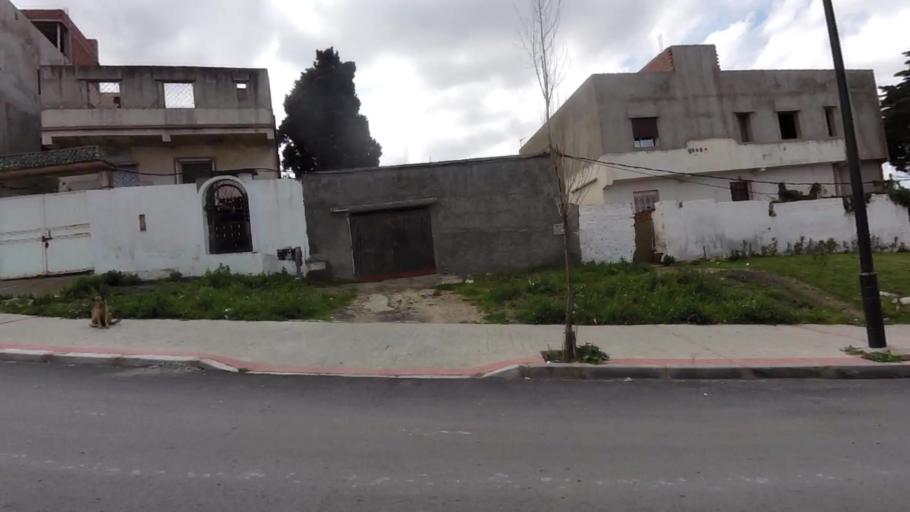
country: MA
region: Tanger-Tetouan
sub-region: Tanger-Assilah
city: Tangier
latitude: 35.7796
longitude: -5.7548
